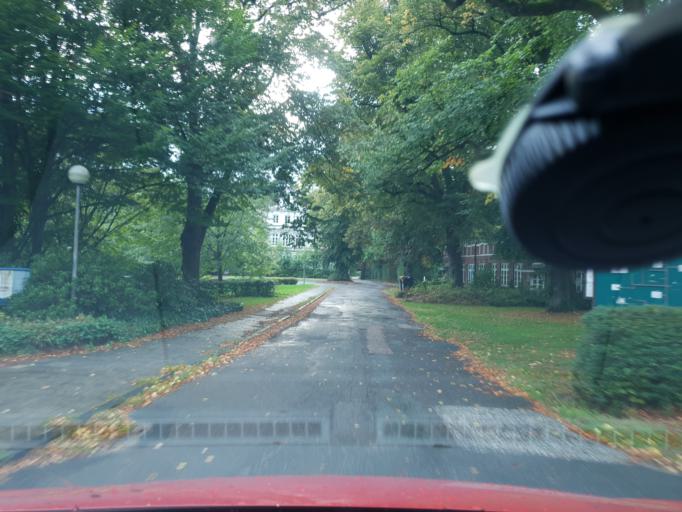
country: DE
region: Schleswig-Holstein
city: Molfsee
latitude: 54.2904
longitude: 10.0855
